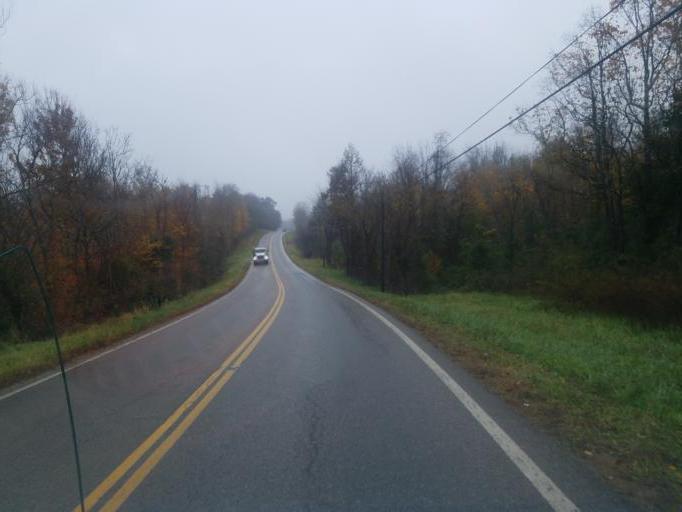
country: US
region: Ohio
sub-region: Morgan County
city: McConnelsville
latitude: 39.5137
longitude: -81.8508
